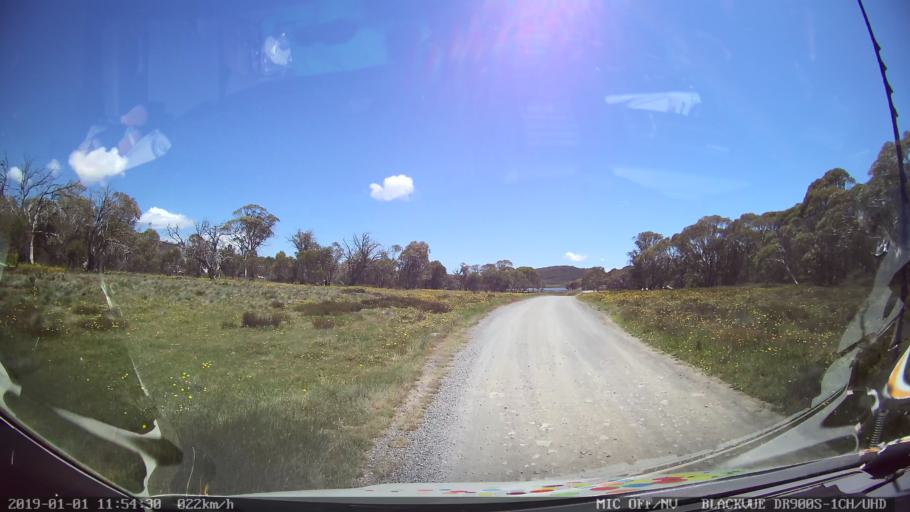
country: AU
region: New South Wales
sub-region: Snowy River
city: Jindabyne
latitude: -35.8911
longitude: 148.4480
